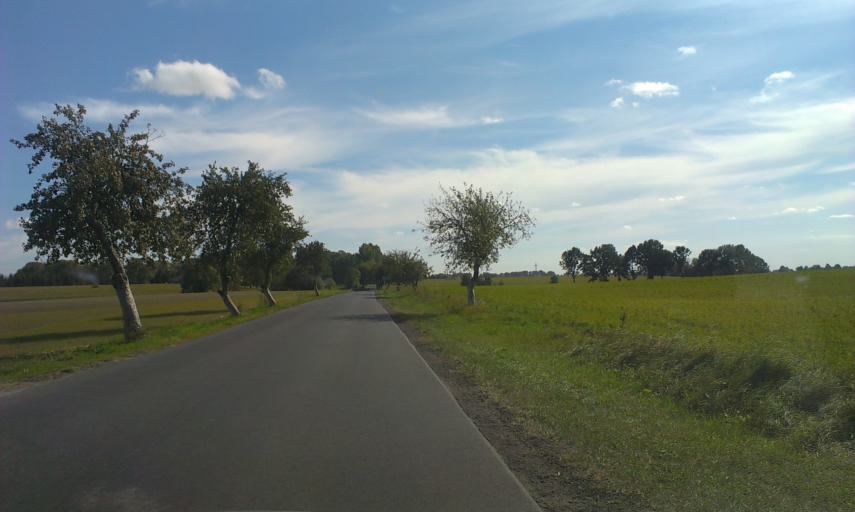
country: PL
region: Greater Poland Voivodeship
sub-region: Powiat pilski
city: Lobzenica
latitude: 53.2728
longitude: 17.2308
